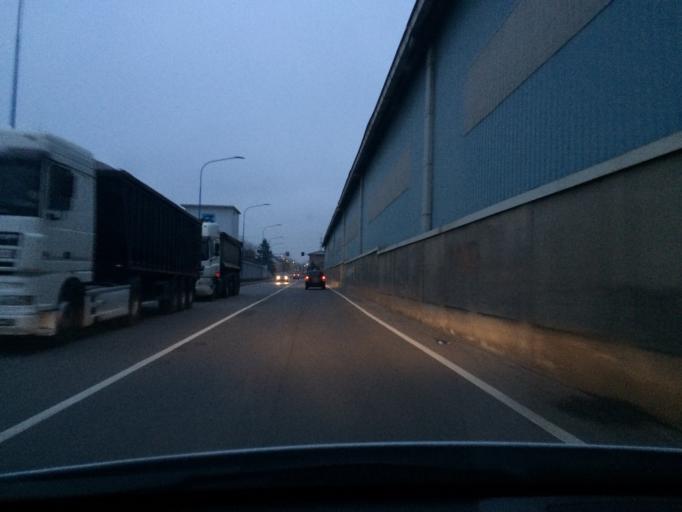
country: IT
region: Lombardy
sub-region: Provincia di Brescia
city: Folzano
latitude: 45.4941
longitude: 10.2108
